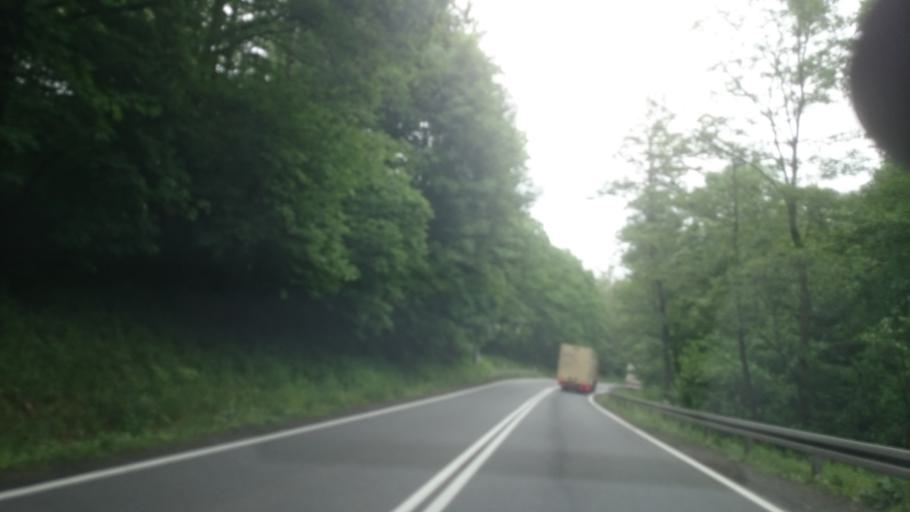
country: PL
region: Lower Silesian Voivodeship
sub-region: Powiat zabkowicki
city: Zloty Stok
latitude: 50.4367
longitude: 16.8223
